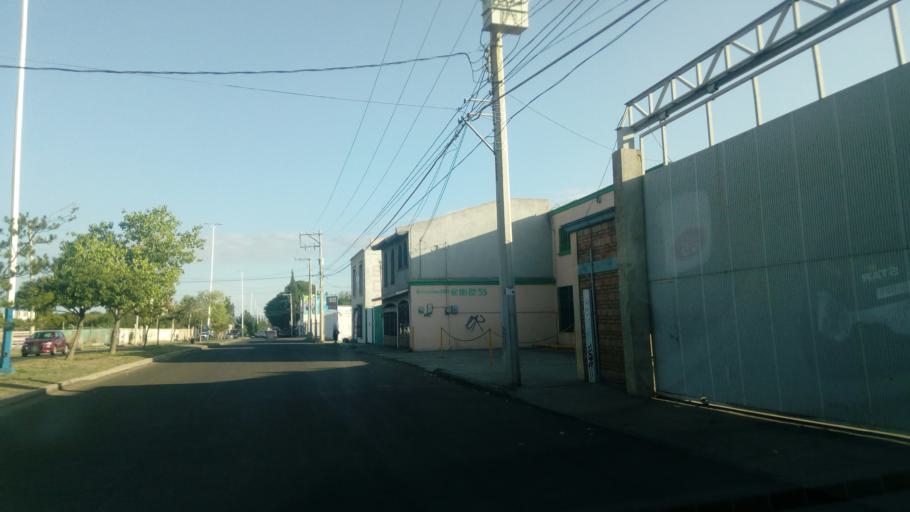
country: MX
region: Durango
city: Victoria de Durango
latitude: 24.0409
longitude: -104.6101
